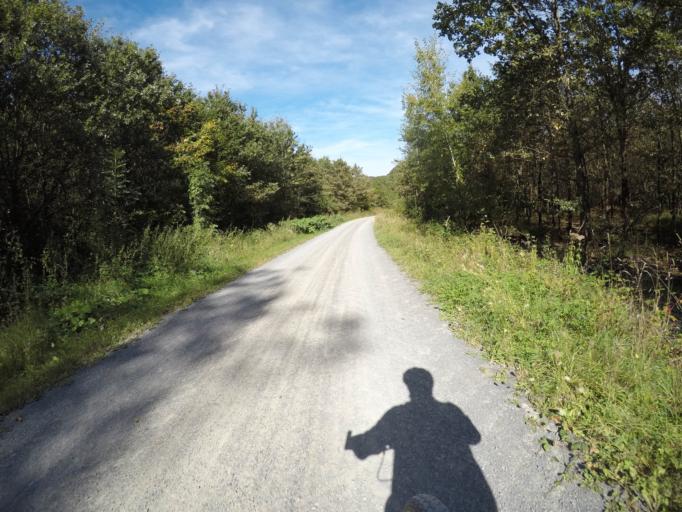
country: DE
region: Baden-Wuerttemberg
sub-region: Karlsruhe Region
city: Sternenfels
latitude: 49.0106
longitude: 8.8781
